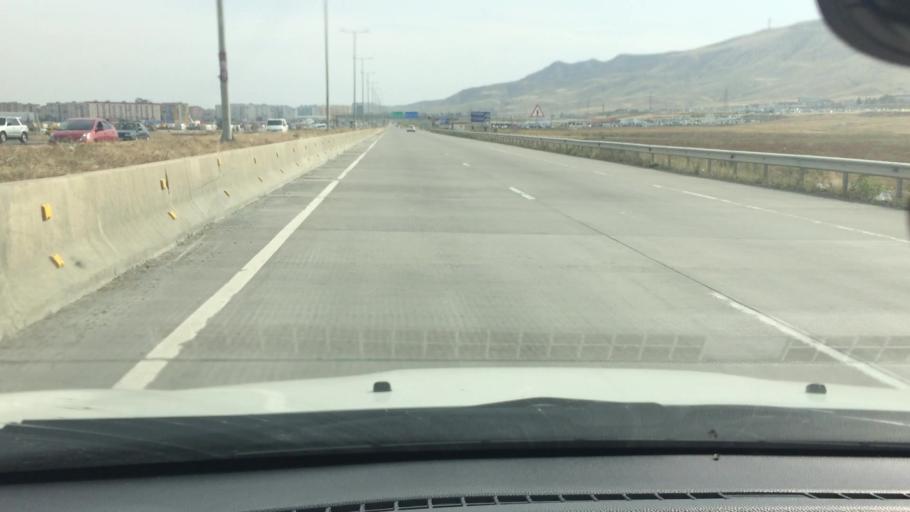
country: GE
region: Kvemo Kartli
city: Rust'avi
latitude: 41.5797
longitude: 44.9541
